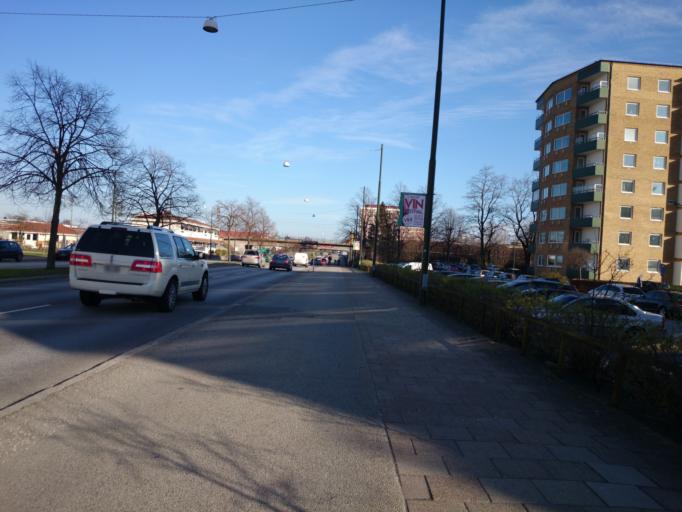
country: SE
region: Skane
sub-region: Malmo
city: Malmoe
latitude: 55.6020
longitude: 13.0346
